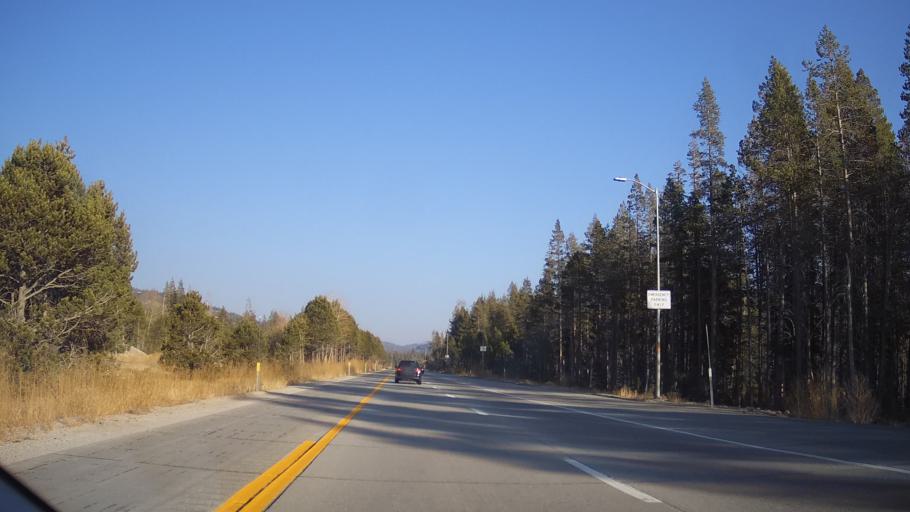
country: US
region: California
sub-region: Nevada County
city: Truckee
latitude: 39.3118
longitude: -120.4884
